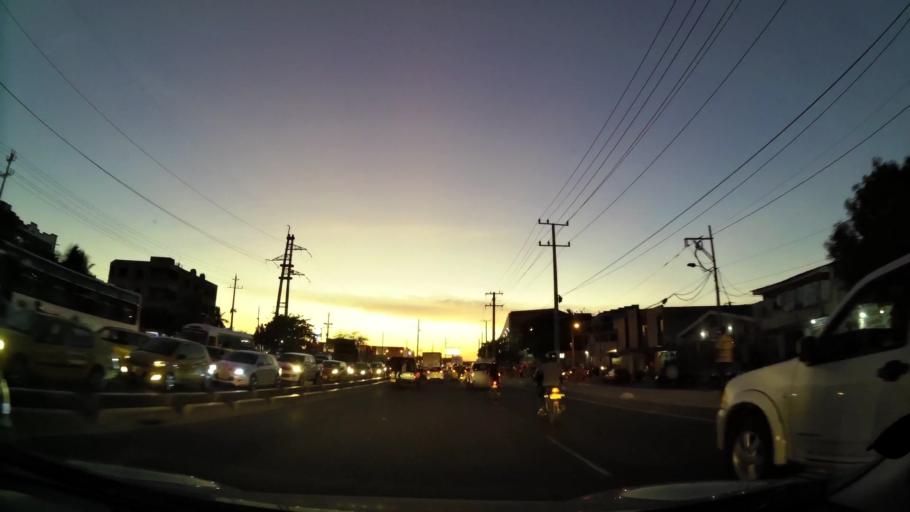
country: CO
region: Atlantico
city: Soledad
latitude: 10.9239
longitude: -74.7949
